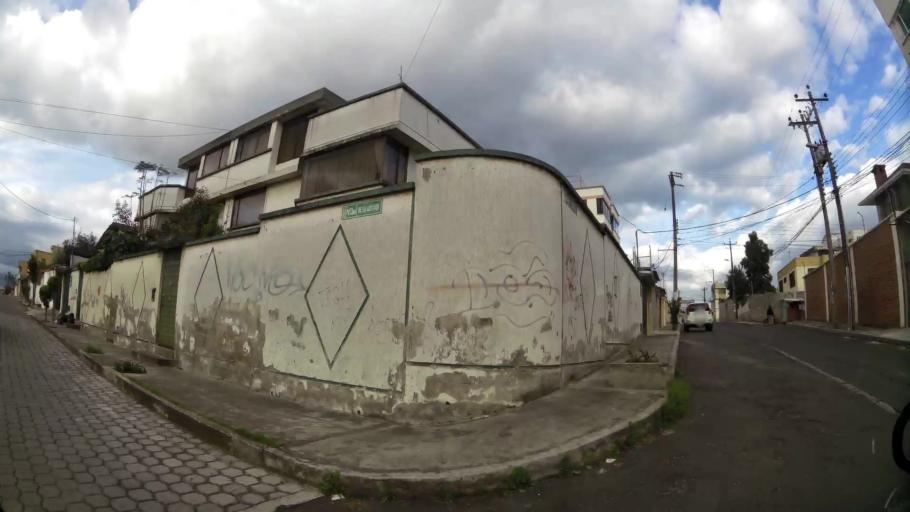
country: EC
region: Pichincha
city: Quito
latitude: -0.1332
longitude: -78.4645
